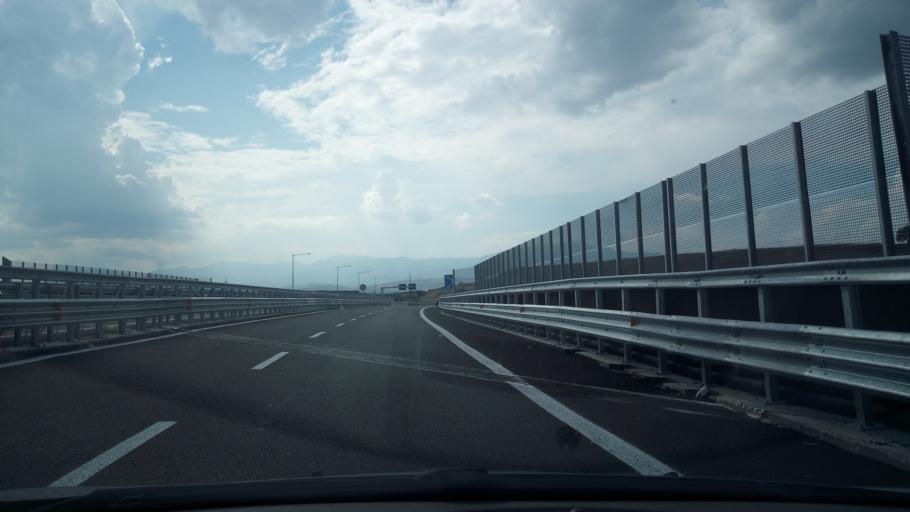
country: IT
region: Calabria
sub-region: Provincia di Cosenza
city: Doria
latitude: 39.7235
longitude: 16.3124
